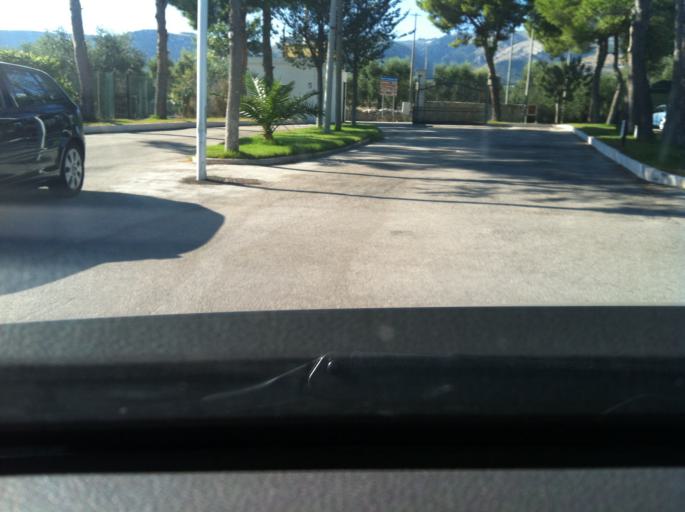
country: IT
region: Apulia
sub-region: Provincia di Foggia
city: Monte Sant'Angelo
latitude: 41.6585
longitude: 15.9758
